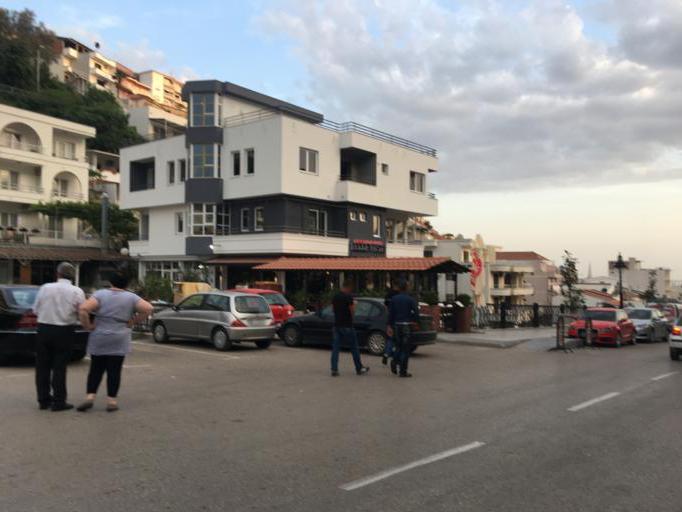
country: ME
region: Ulcinj
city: Ulcinj
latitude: 41.9271
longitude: 19.2056
